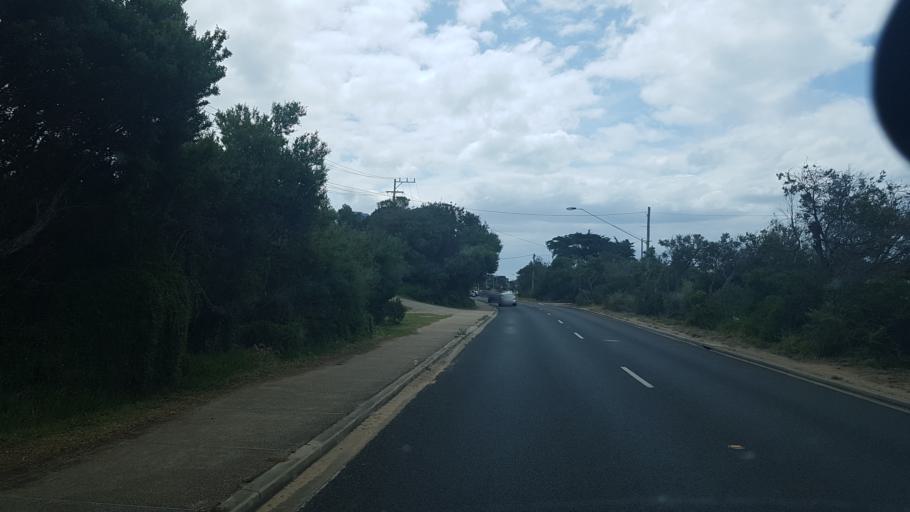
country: AU
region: Victoria
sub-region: Mornington Peninsula
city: Sorrento
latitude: -38.3427
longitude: 144.7379
